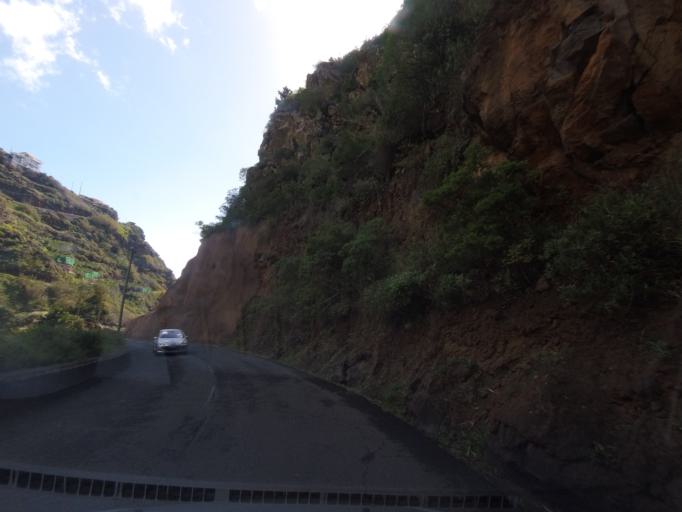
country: PT
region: Madeira
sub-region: Calheta
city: Estreito da Calheta
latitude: 32.7366
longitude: -17.2008
